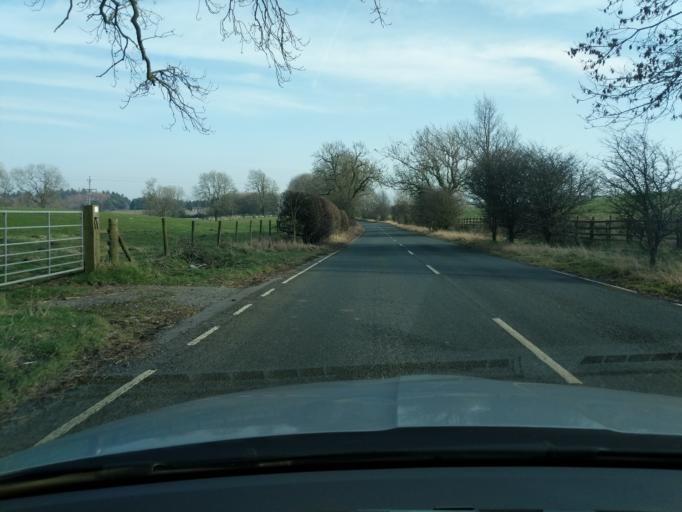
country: GB
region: England
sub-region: North Yorkshire
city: Catterick Garrison
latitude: 54.3467
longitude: -1.7468
